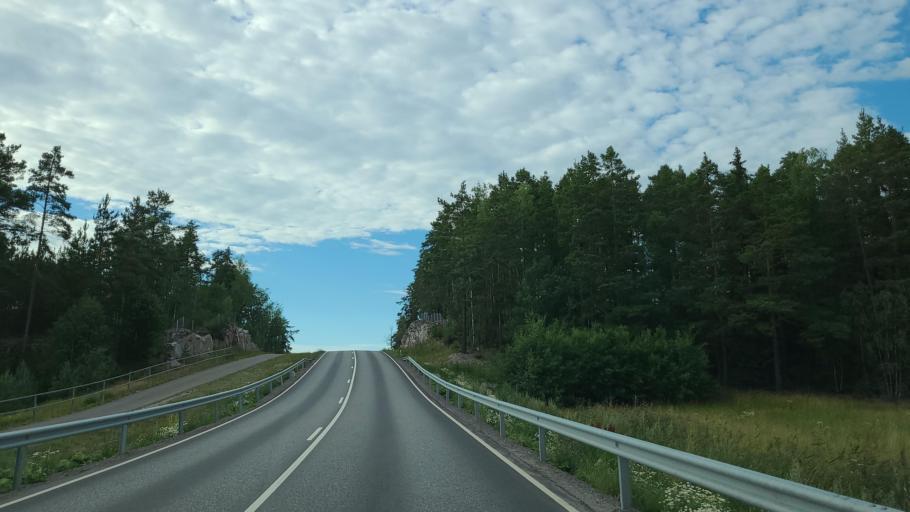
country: FI
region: Varsinais-Suomi
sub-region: Turku
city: Rymaettylae
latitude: 60.3995
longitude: 21.8983
